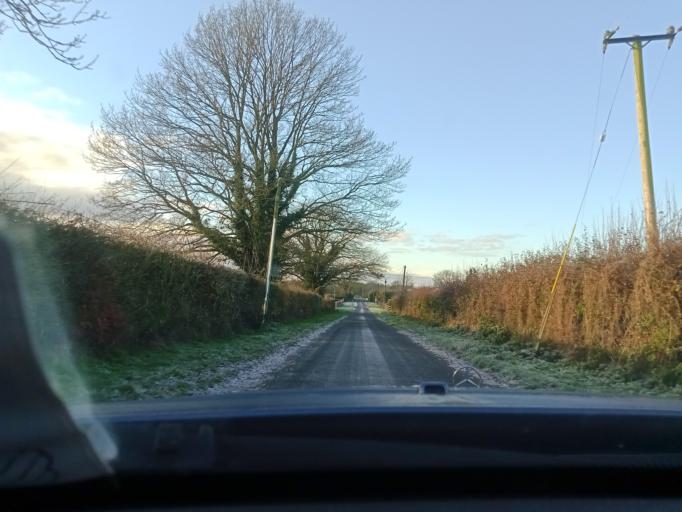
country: IE
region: Leinster
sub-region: County Carlow
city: Bagenalstown
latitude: 52.6483
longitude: -7.0008
